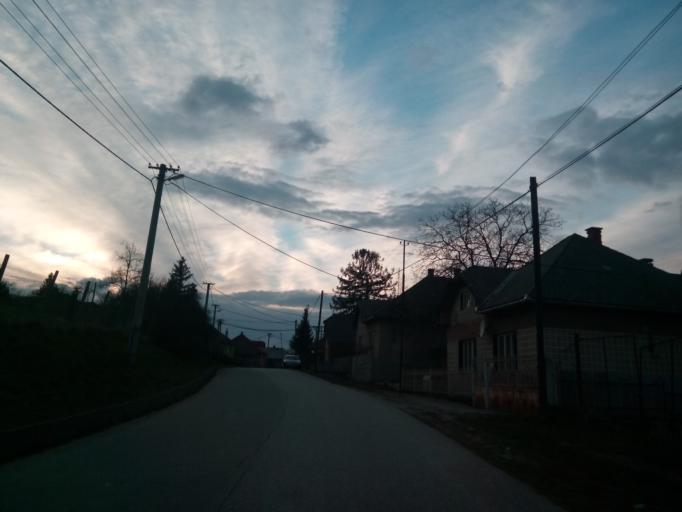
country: SK
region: Kosicky
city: Moldava nad Bodvou
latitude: 48.5572
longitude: 20.9644
